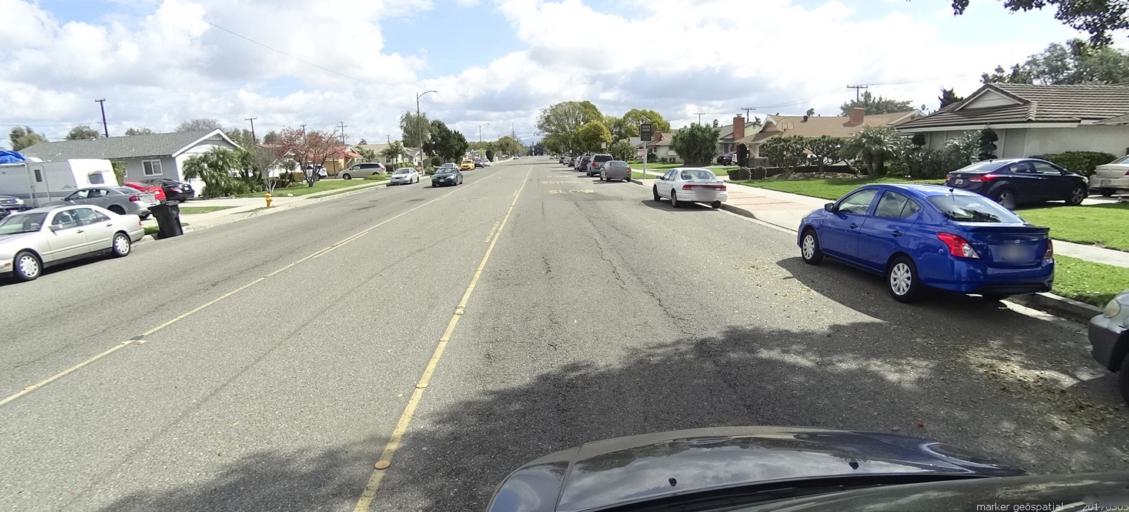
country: US
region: California
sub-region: Orange County
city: Anaheim
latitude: 33.8106
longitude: -117.9367
